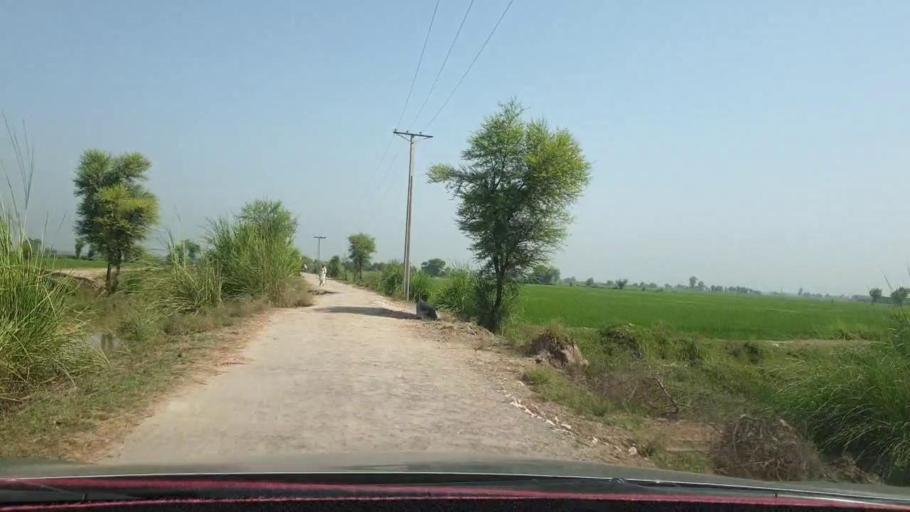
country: PK
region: Sindh
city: Warah
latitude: 27.4895
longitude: 67.8348
